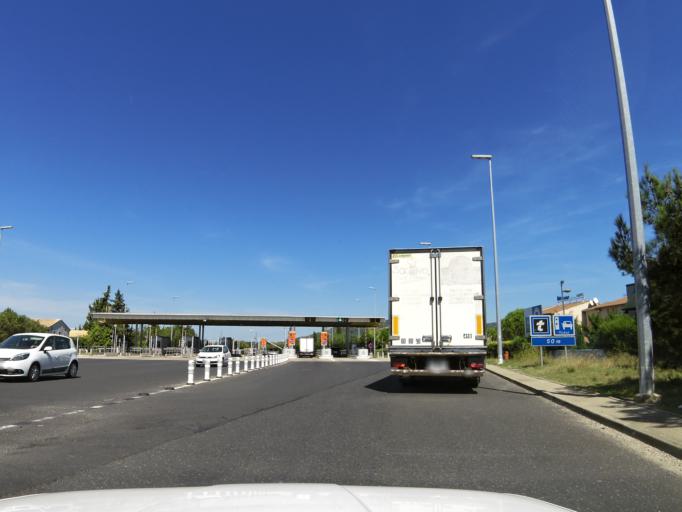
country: FR
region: Provence-Alpes-Cote d'Azur
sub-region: Departement du Vaucluse
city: Bollene
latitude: 44.2895
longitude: 4.7510
